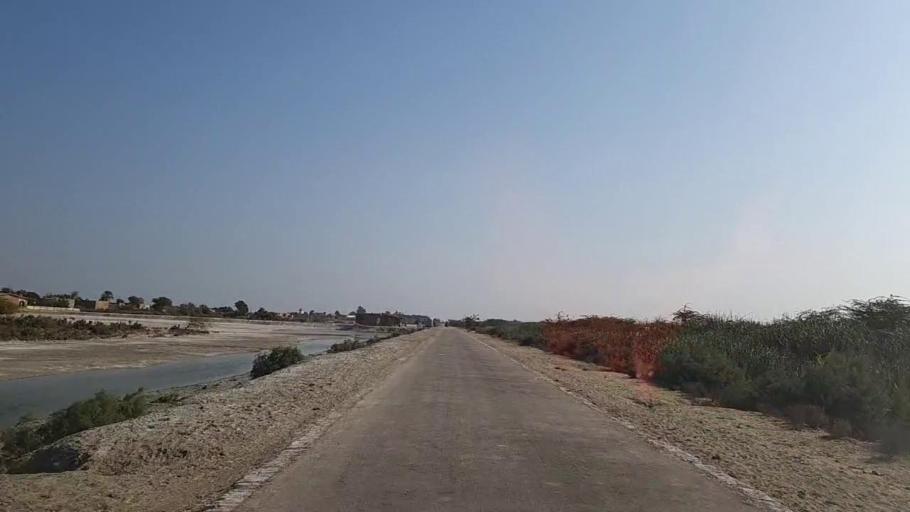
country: PK
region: Sindh
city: Tando Mittha Khan
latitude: 25.9343
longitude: 69.0598
